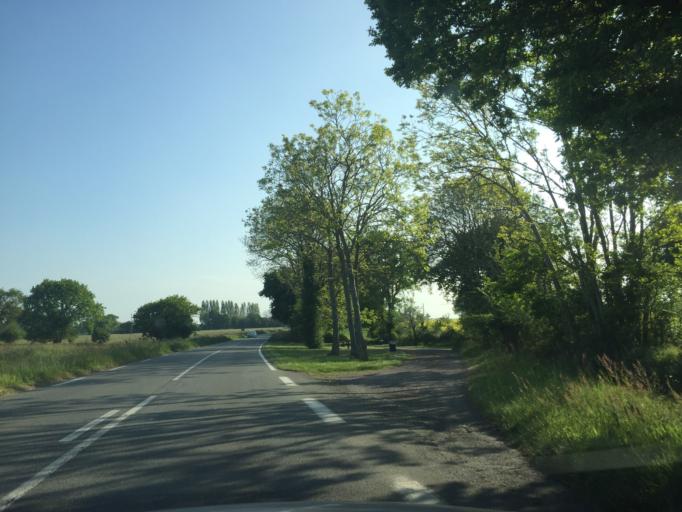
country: FR
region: Brittany
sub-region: Departement des Cotes-d'Armor
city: Saint-Cast-le-Guildo
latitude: 48.6116
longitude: -2.2725
